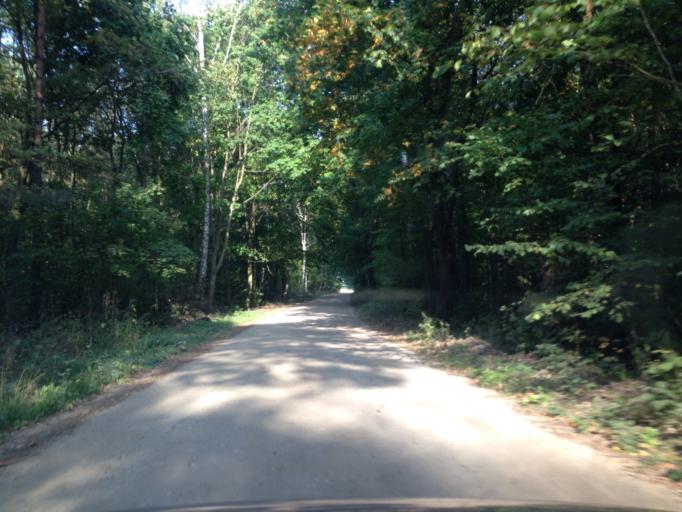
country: PL
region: Kujawsko-Pomorskie
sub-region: Powiat brodnicki
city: Gorzno
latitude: 53.2187
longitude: 19.6412
